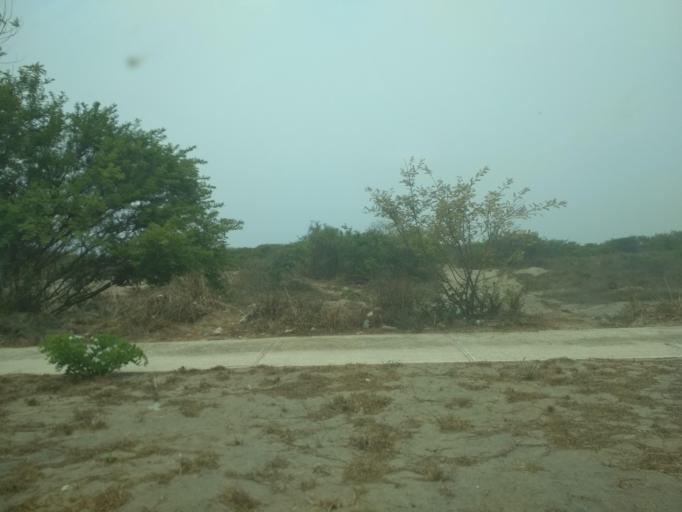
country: MX
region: Veracruz
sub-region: Alvarado
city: Playa de la Libertad
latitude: 19.0600
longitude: -96.0716
